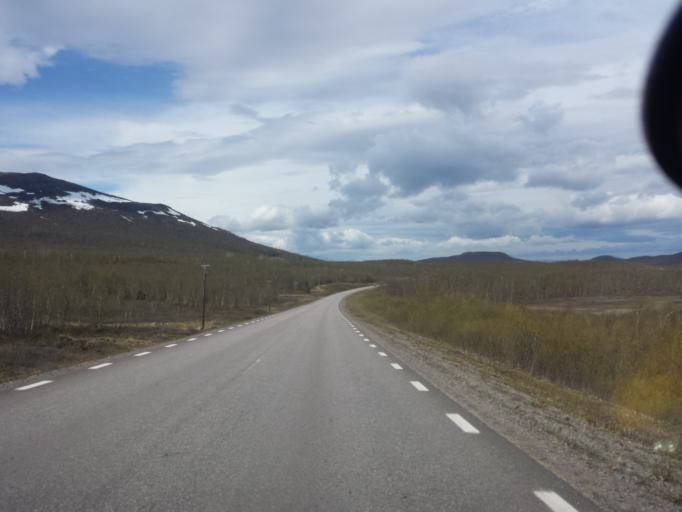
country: SE
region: Norrbotten
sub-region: Kiruna Kommun
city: Kiruna
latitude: 68.1603
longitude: 19.7787
